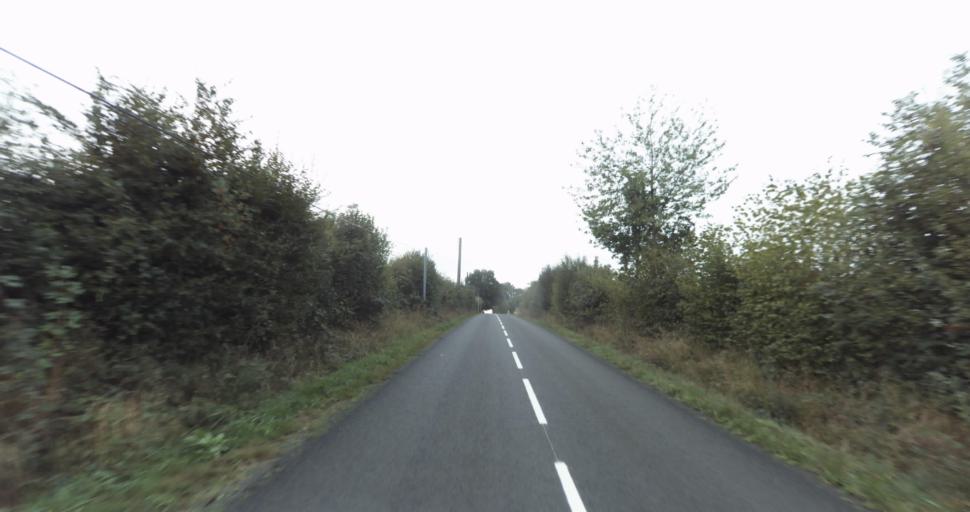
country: FR
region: Lower Normandy
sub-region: Departement de l'Orne
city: Sainte-Gauburge-Sainte-Colombe
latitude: 48.7469
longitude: 0.4377
